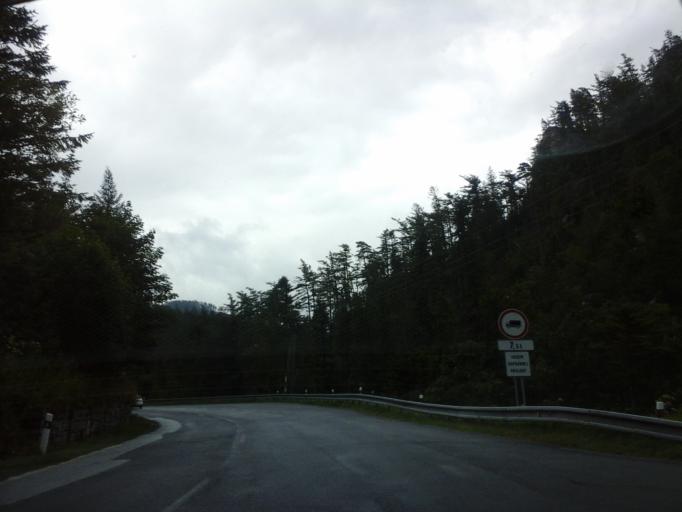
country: SK
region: Presovsky
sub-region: Okres Poprad
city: Zdiar
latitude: 49.2311
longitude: 20.3158
